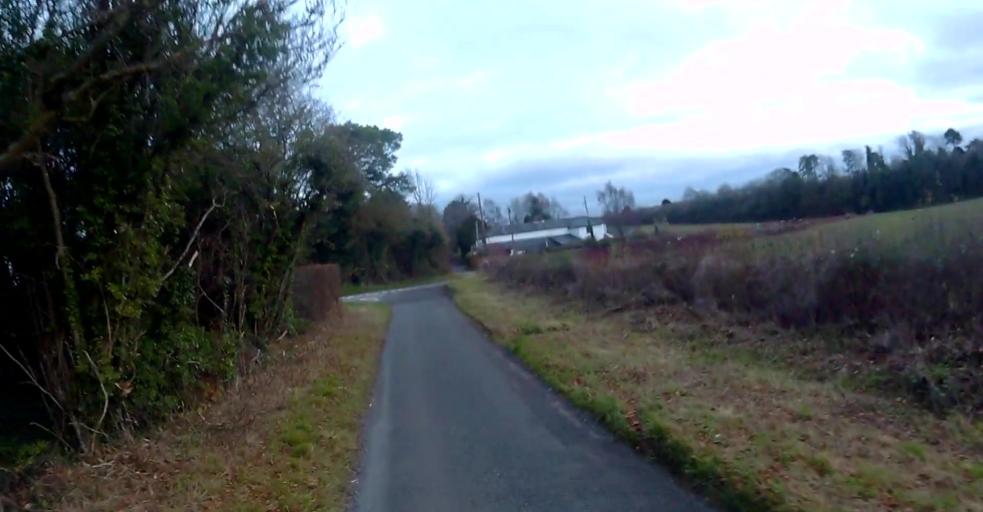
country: GB
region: England
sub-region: Hampshire
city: Overton
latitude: 51.2577
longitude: -1.2319
